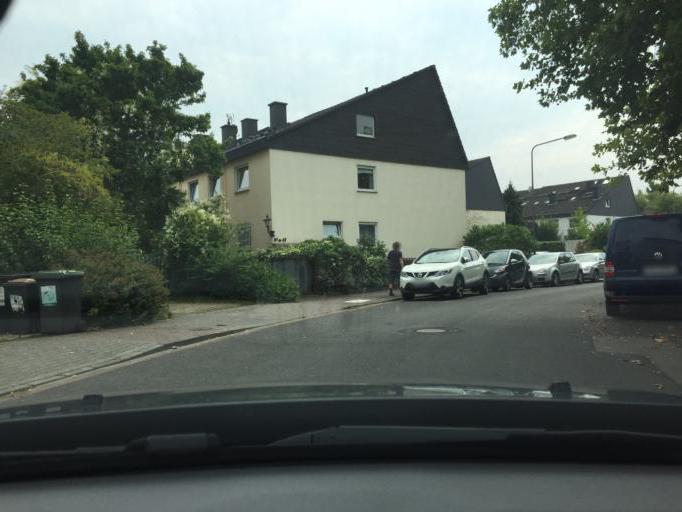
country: DE
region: Hesse
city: Kelsterbach
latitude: 50.0860
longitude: 8.5729
